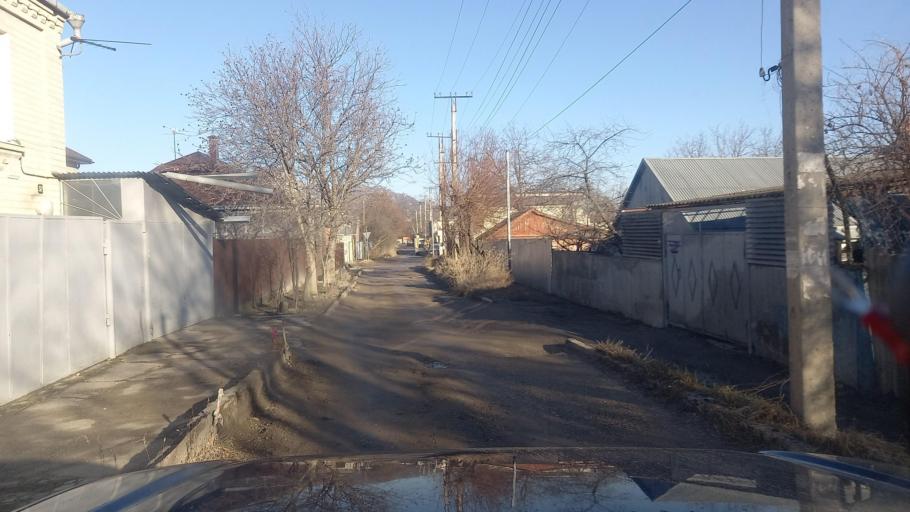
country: RU
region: Stavropol'skiy
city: Svobody
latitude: 44.0227
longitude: 43.0498
